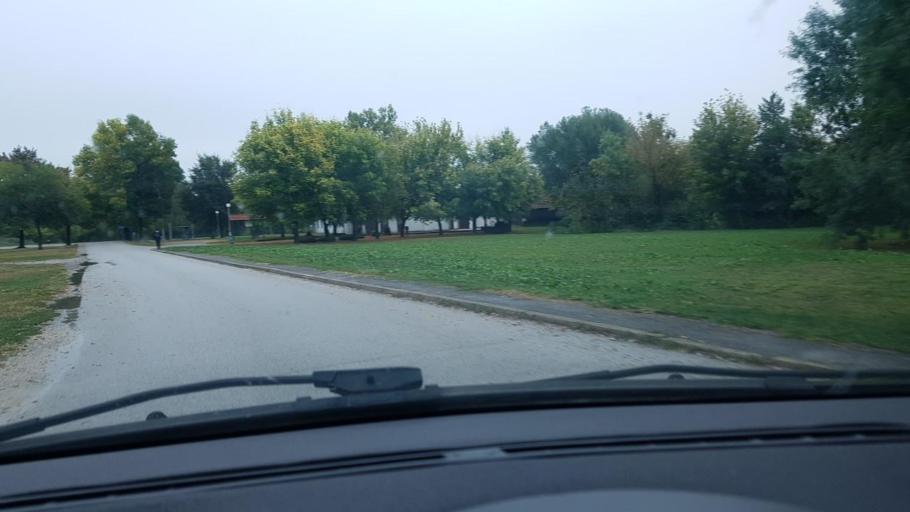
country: HR
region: Krapinsko-Zagorska
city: Bedekovcina
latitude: 46.0410
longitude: 16.0027
